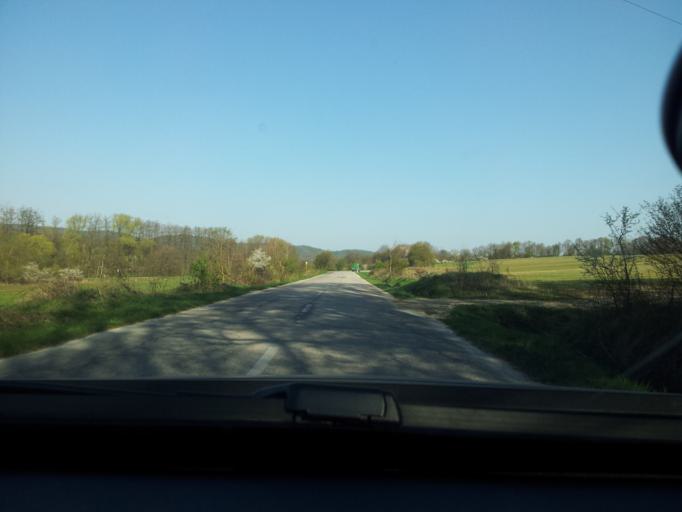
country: SK
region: Nitriansky
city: Partizanske
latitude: 48.5319
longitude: 18.3635
